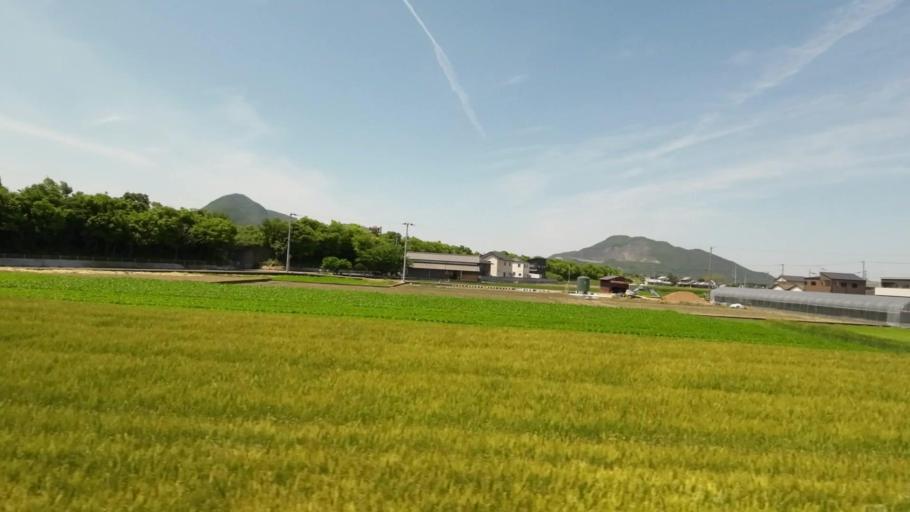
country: JP
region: Kagawa
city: Marugame
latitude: 34.2436
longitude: 133.7806
